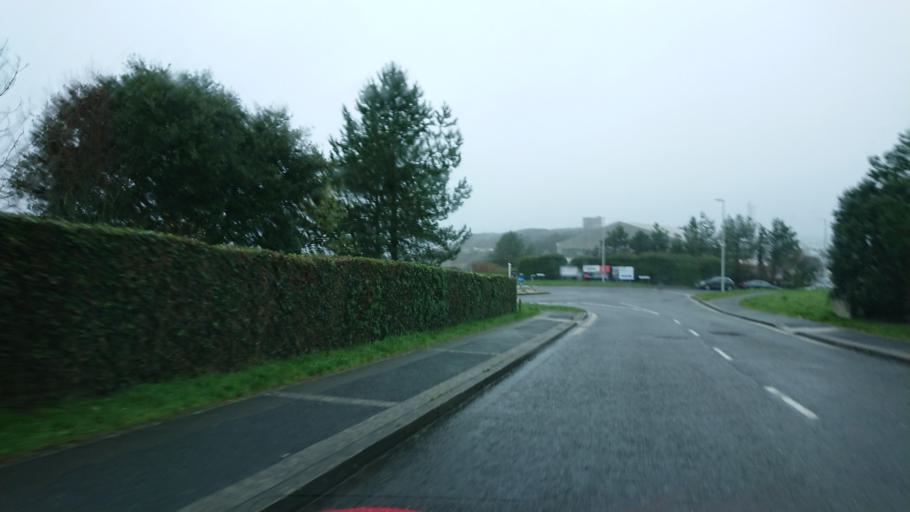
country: GB
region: England
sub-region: Plymouth
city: Plymouth
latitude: 50.3572
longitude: -4.1245
